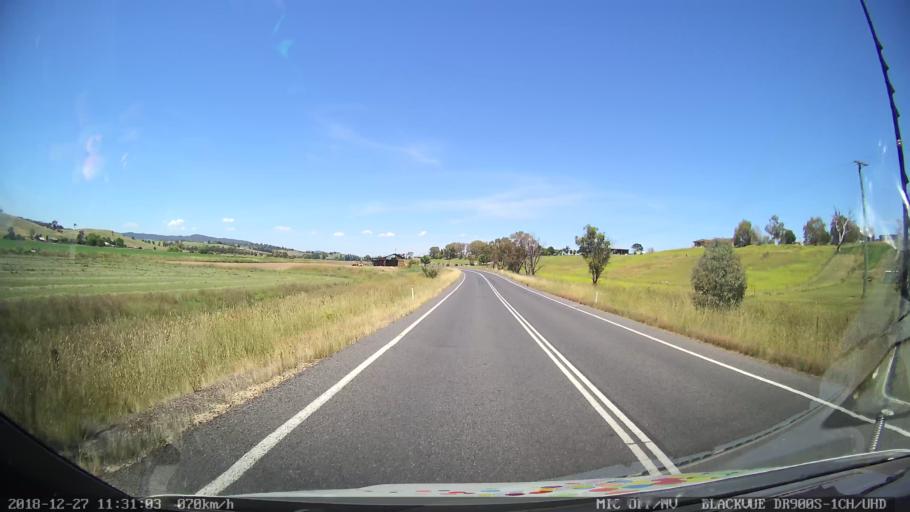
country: AU
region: New South Wales
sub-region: Bathurst Regional
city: Perthville
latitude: -33.4912
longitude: 149.5412
